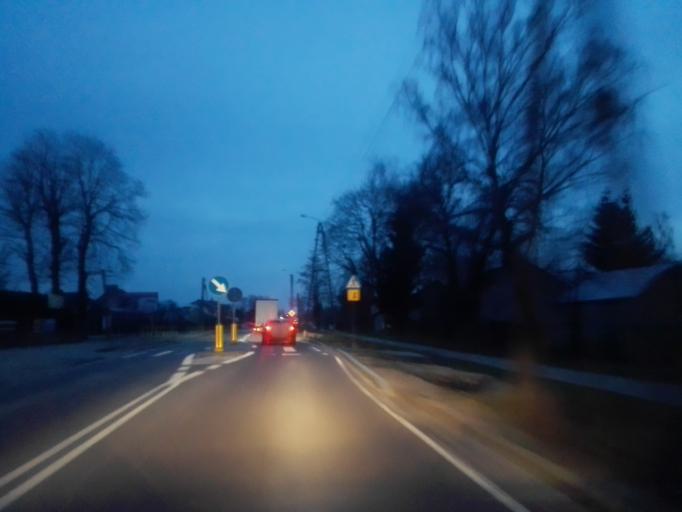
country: PL
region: Podlasie
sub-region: Lomza
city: Lomza
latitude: 53.1381
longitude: 22.0433
